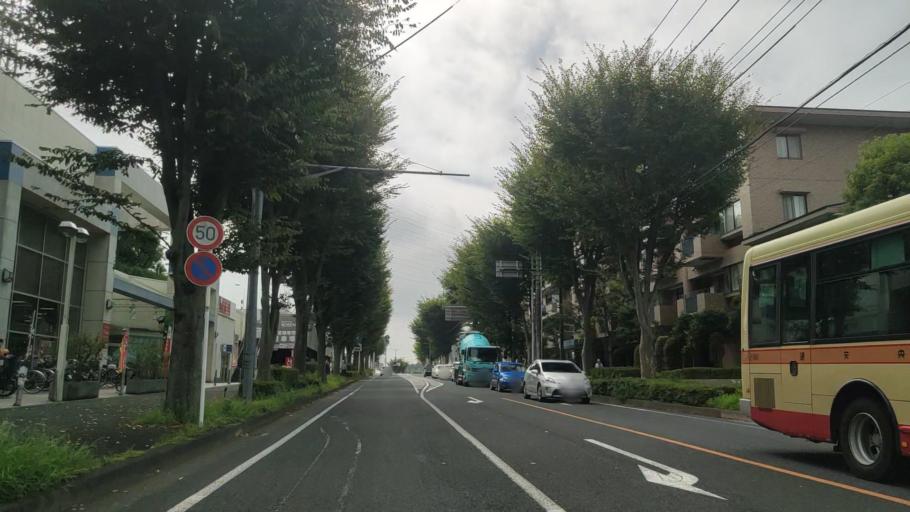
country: JP
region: Kanagawa
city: Fujisawa
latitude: 35.4177
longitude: 139.5230
